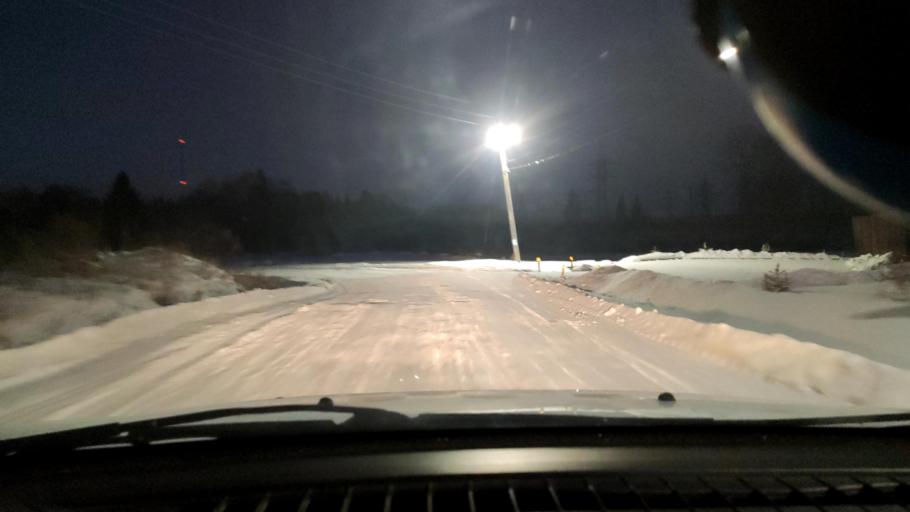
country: RU
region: Perm
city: Kultayevo
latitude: 57.9221
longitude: 55.8671
